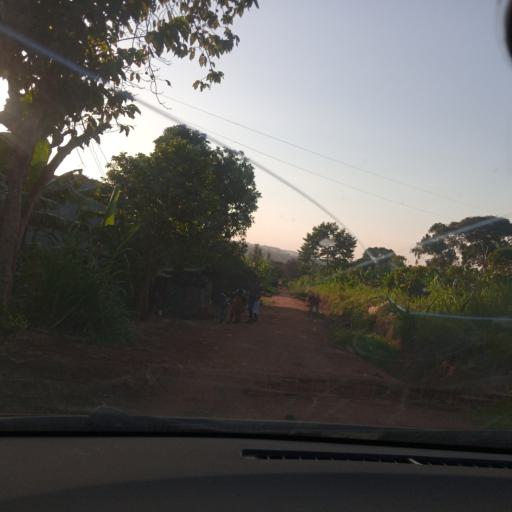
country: UG
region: Central Region
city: Masaka
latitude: -0.3352
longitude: 31.7571
